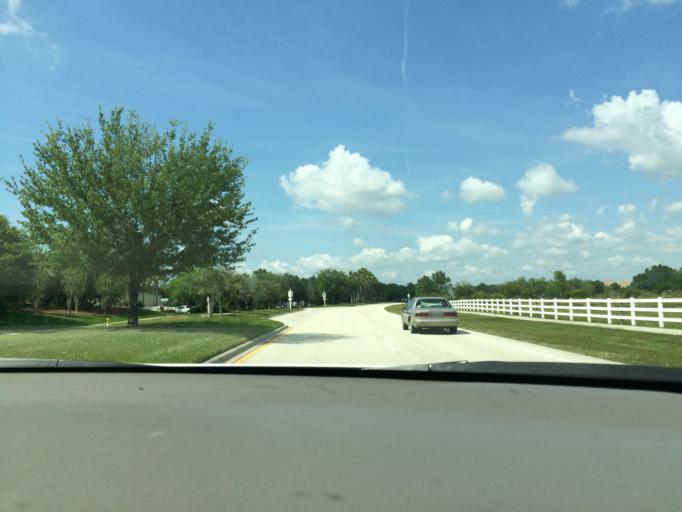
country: US
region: Florida
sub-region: Sarasota County
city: The Meadows
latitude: 27.4009
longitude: -82.3992
